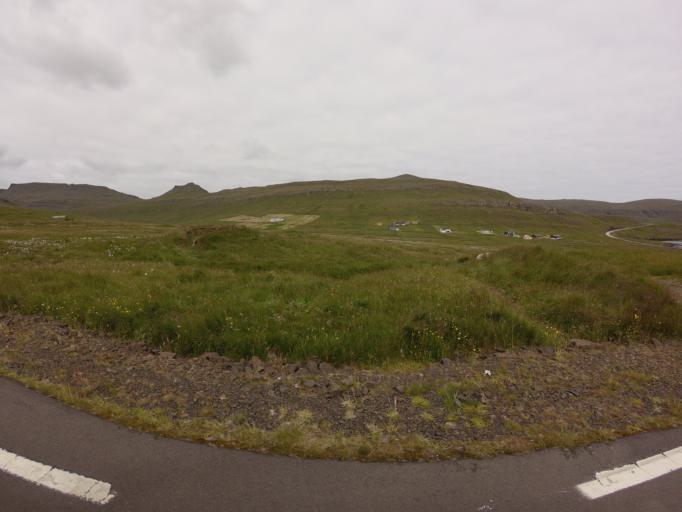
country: FO
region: Suduroy
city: Tvoroyri
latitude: 61.5309
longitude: -6.8200
